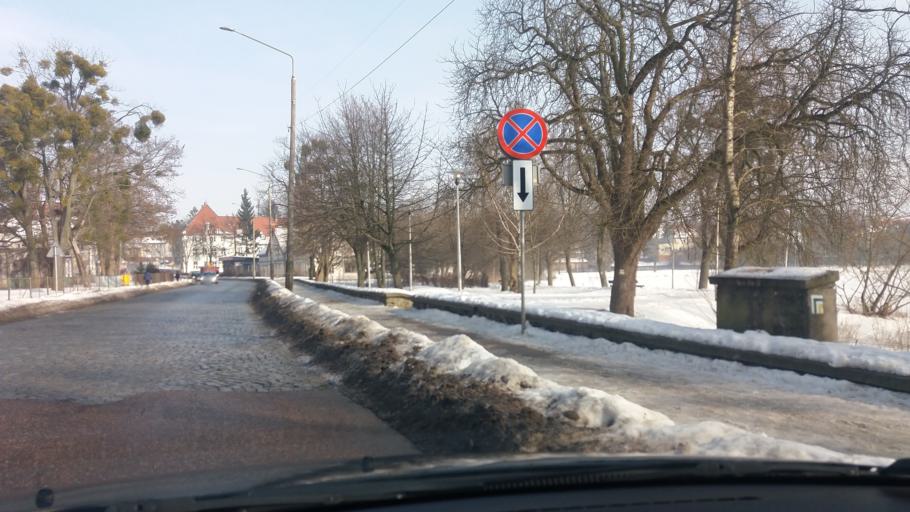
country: PL
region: Warmian-Masurian Voivodeship
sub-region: Powiat szczycienski
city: Szczytno
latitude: 53.5683
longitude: 20.9909
